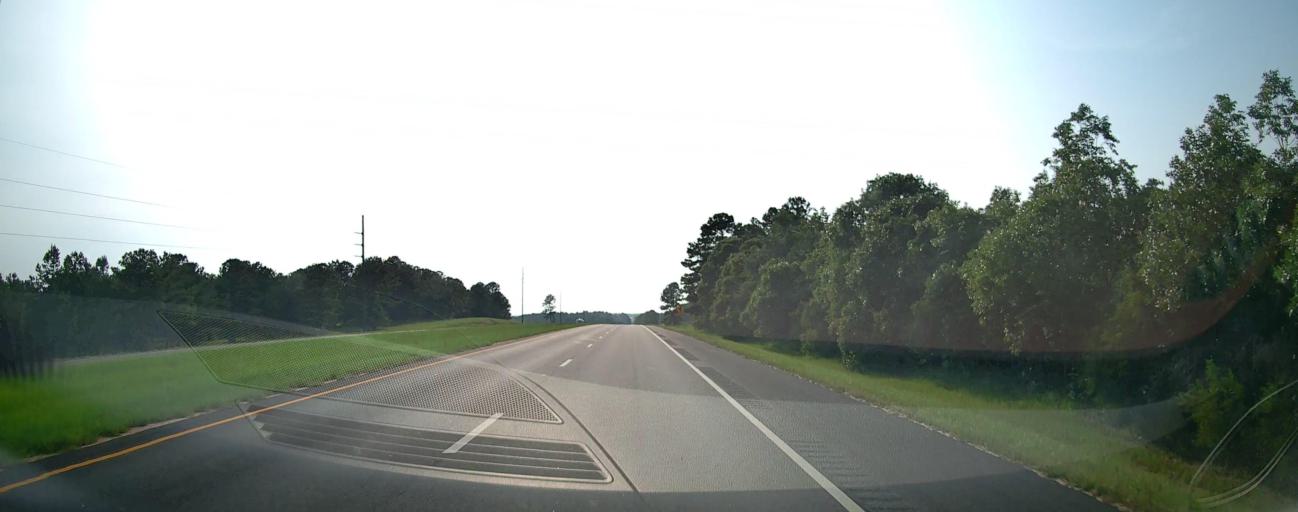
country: US
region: Georgia
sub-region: Taylor County
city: Butler
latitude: 32.5869
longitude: -84.3468
